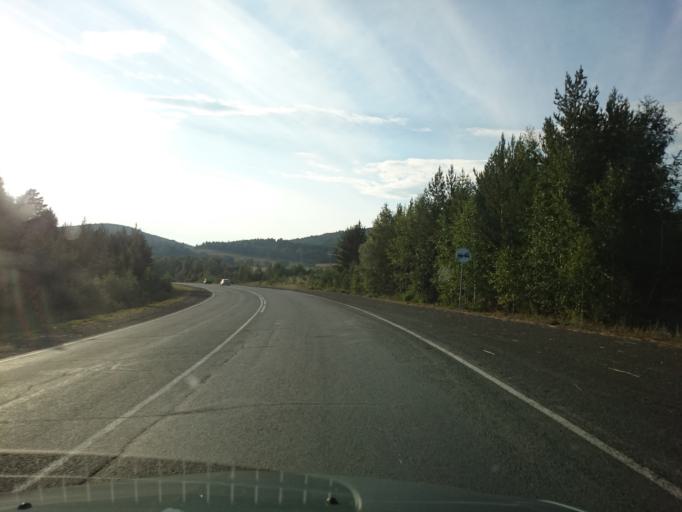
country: RU
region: Bashkortostan
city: Lomovka
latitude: 53.8956
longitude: 58.0912
